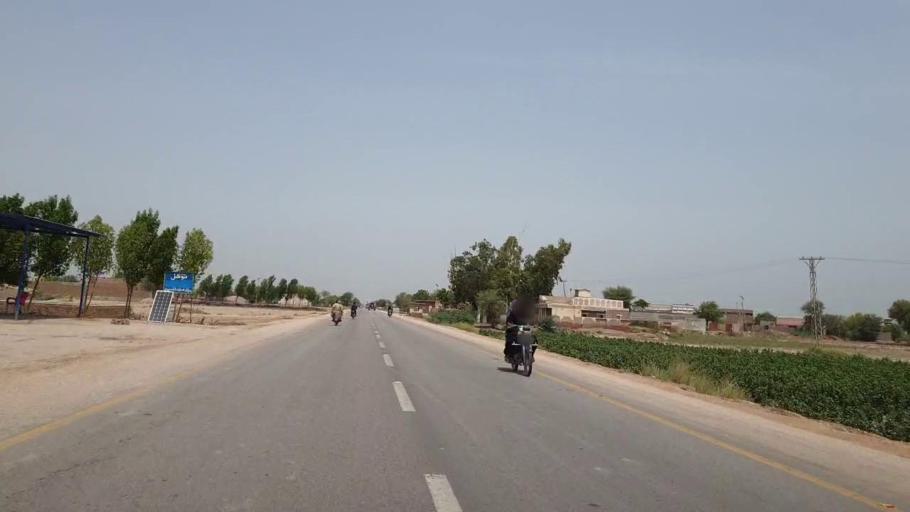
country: PK
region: Sindh
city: Shahpur Chakar
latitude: 26.1684
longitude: 68.6213
